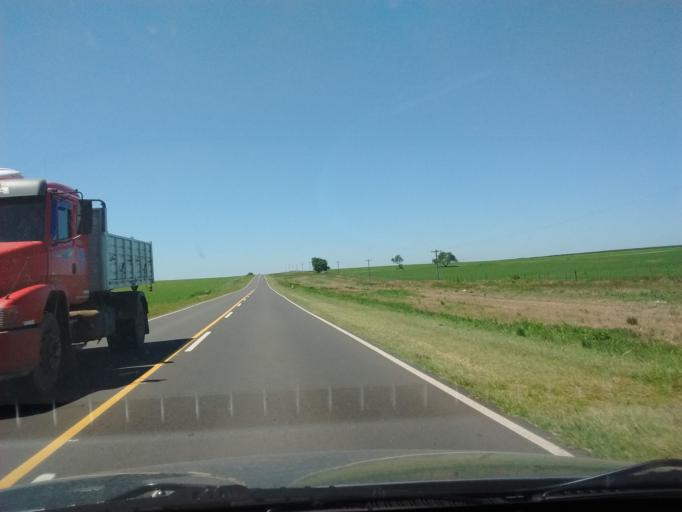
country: AR
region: Entre Rios
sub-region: Departamento de Victoria
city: Victoria
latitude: -32.7955
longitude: -59.8965
